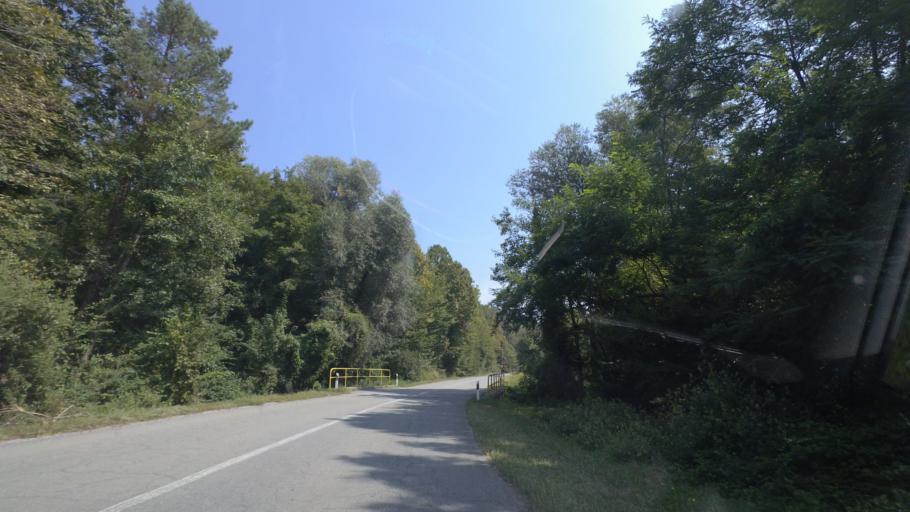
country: HR
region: Sisacko-Moslavacka
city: Glina
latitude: 45.2276
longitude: 16.1364
